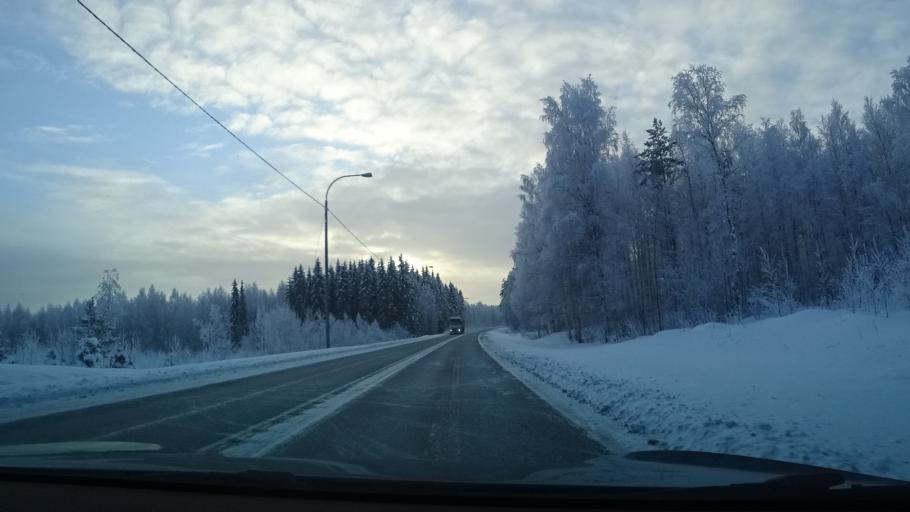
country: FI
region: North Karelia
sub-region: Joensuu
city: Pyhaeselkae
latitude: 62.4609
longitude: 30.0038
